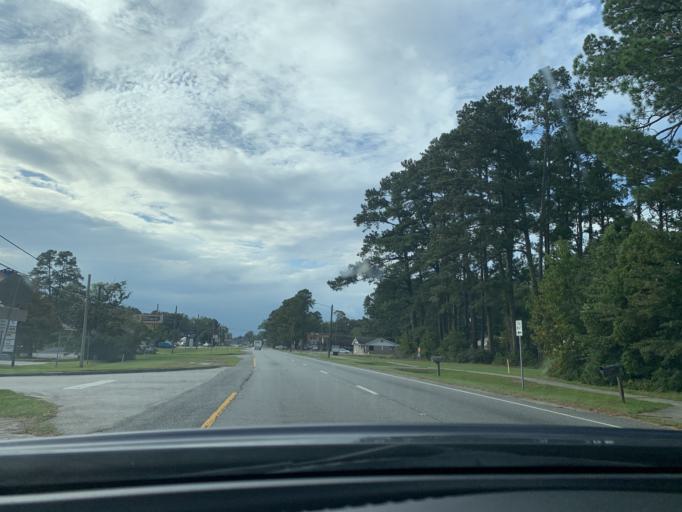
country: US
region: Georgia
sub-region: Chatham County
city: Pooler
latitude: 32.1178
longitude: -81.2537
